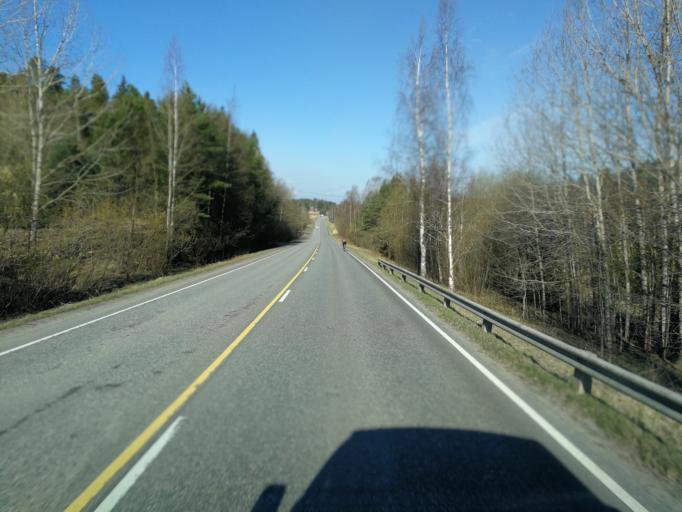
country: FI
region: Uusimaa
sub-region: Helsinki
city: Espoo
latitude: 60.2007
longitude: 24.5464
